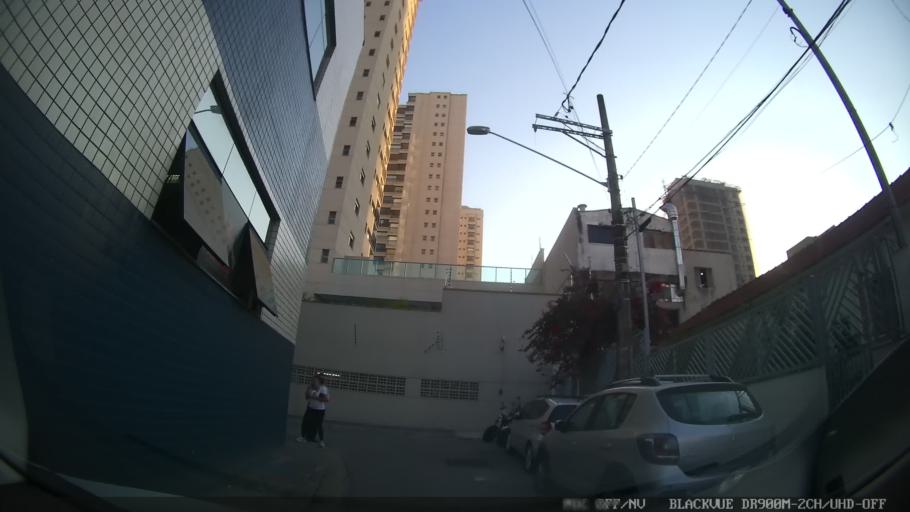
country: BR
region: Sao Paulo
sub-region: Sao Paulo
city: Sao Paulo
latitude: -23.5030
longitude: -46.6403
